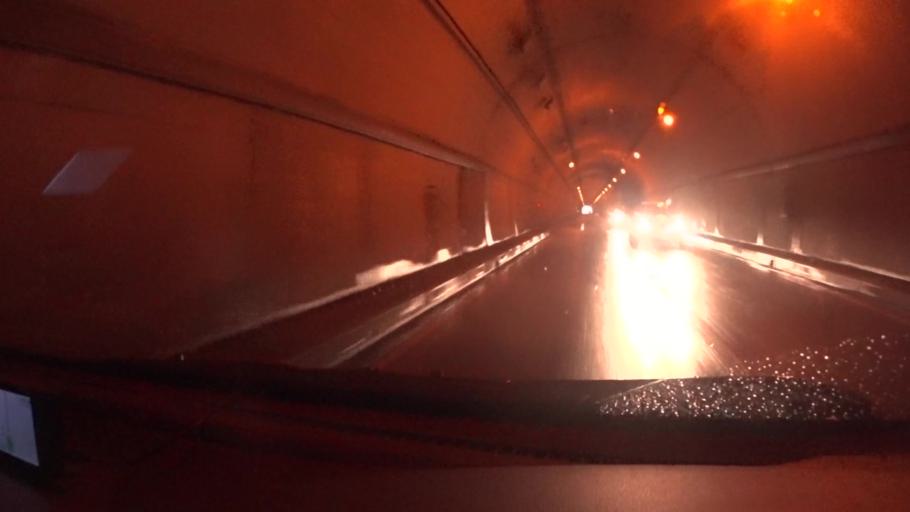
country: JP
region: Kyoto
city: Ayabe
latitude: 35.2410
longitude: 135.3163
